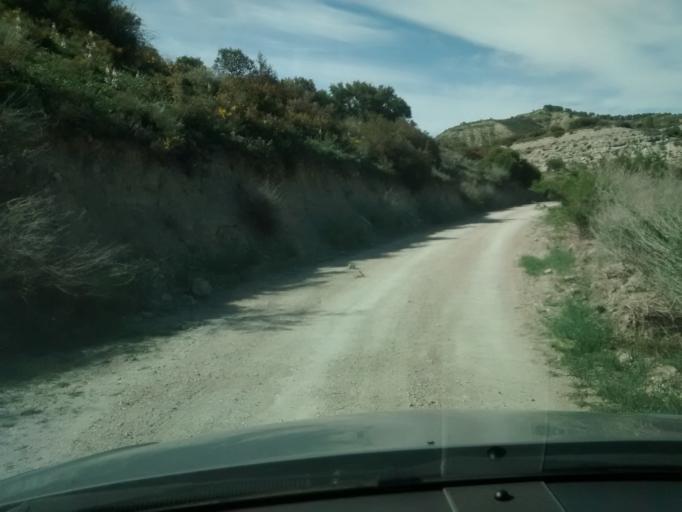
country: ES
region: Aragon
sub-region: Provincia de Huesca
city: Alcubierre
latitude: 41.8172
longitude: -0.5114
